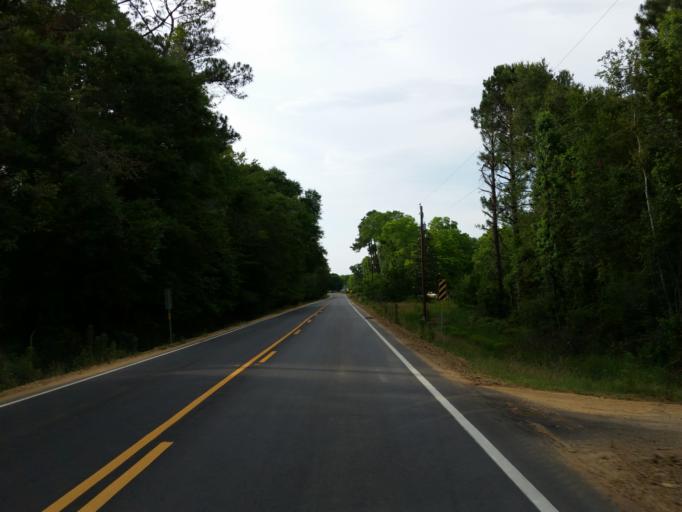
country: US
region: Georgia
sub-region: Turner County
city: Ashburn
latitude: 31.7623
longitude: -83.6844
